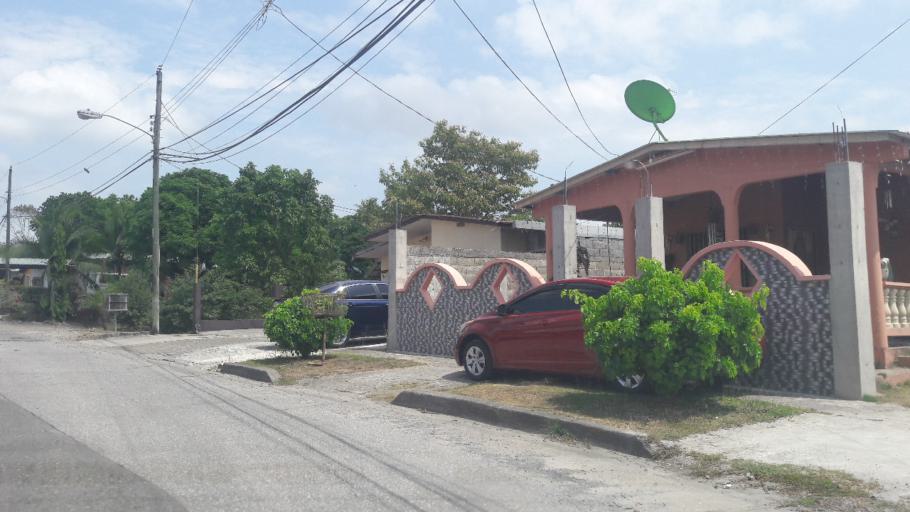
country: PA
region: Panama
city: Alcalde Diaz
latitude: 9.1368
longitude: -79.5506
